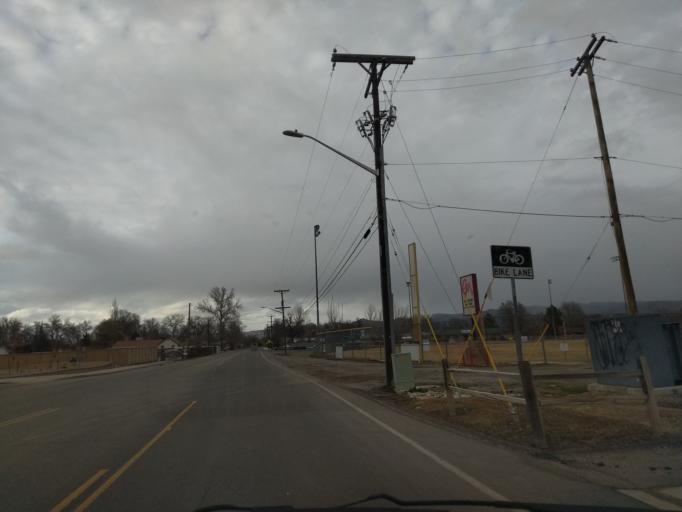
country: US
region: Colorado
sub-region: Mesa County
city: Fruitvale
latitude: 39.0794
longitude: -108.5198
